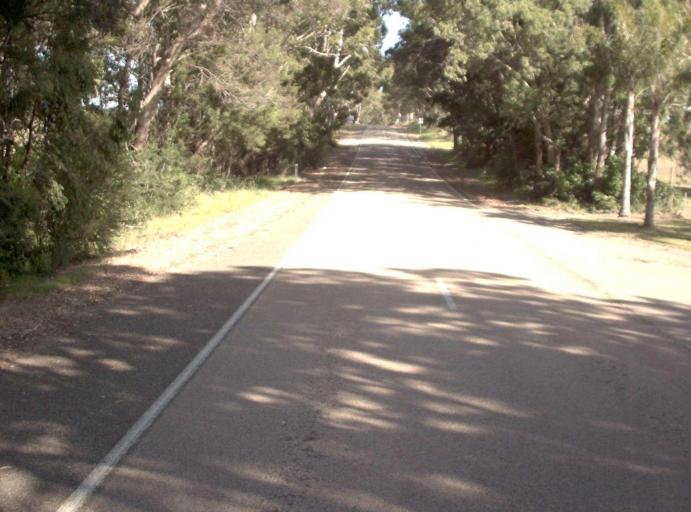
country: AU
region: Victoria
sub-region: East Gippsland
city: Lakes Entrance
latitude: -37.8195
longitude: 147.8538
